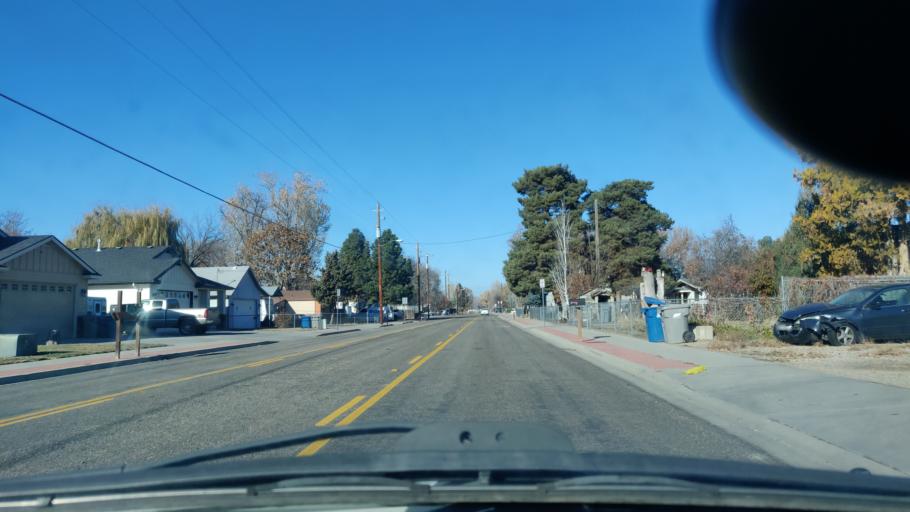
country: US
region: Idaho
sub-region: Ada County
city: Garden City
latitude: 43.6410
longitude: -116.2563
